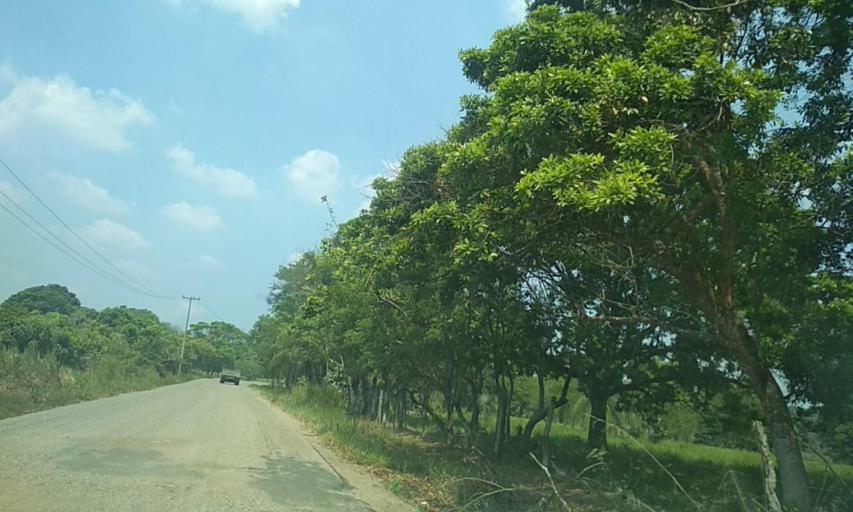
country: MX
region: Tabasco
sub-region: Huimanguillo
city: C-41 (Licenciado Carlos A. Madrazo)
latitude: 17.8300
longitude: -93.5098
